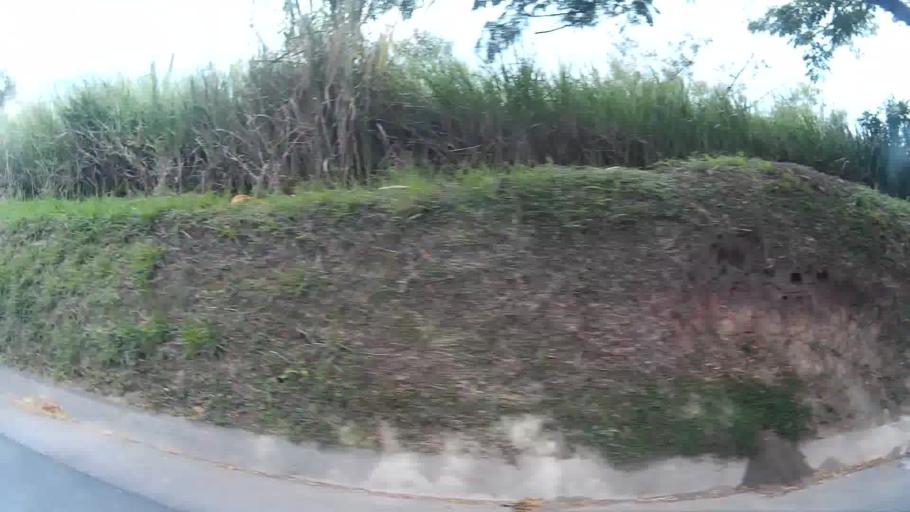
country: CO
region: Risaralda
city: Pereira
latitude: 4.8133
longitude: -75.7996
